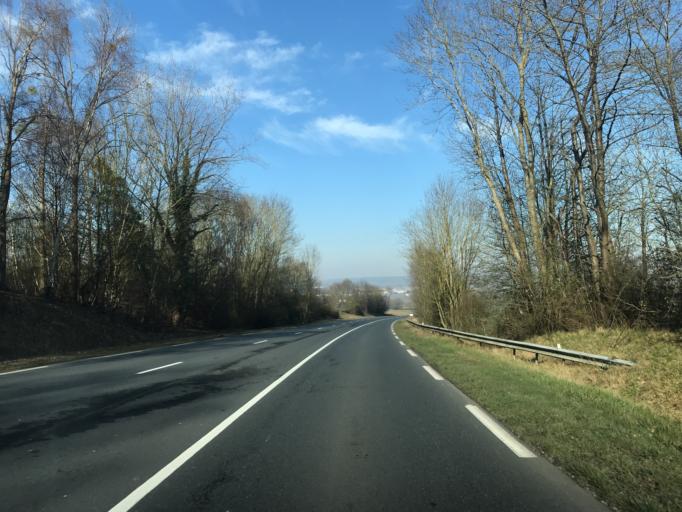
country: FR
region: Haute-Normandie
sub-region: Departement de l'Eure
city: Saint-Pierre-du-Vauvray
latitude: 49.2329
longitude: 1.2058
